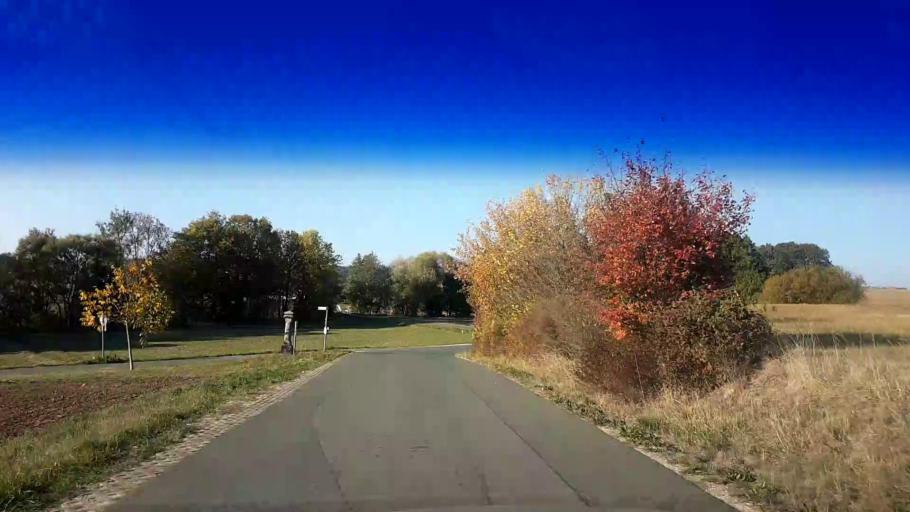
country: DE
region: Bavaria
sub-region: Upper Franconia
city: Strullendorf
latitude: 49.8617
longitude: 10.9983
